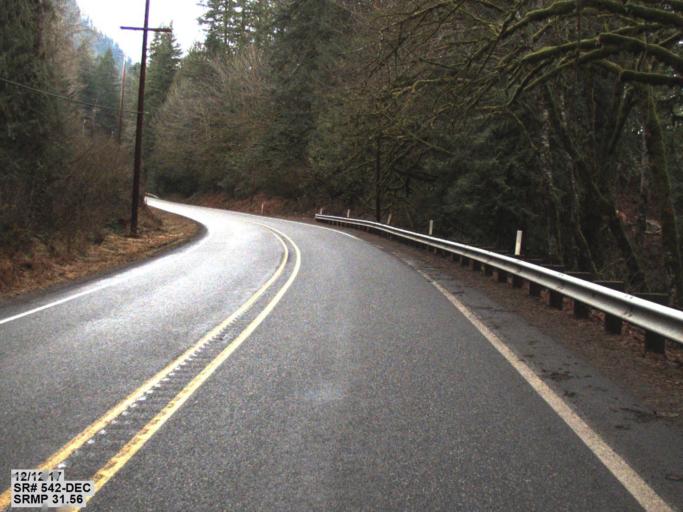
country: US
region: Washington
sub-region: Whatcom County
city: Peaceful Valley
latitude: 48.8997
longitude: -121.9798
